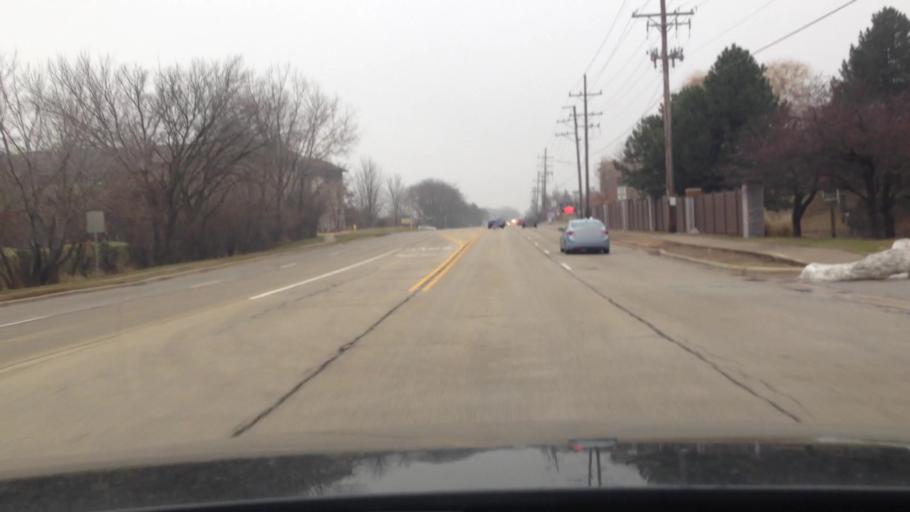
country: US
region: Illinois
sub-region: DuPage County
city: Westmont
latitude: 41.8184
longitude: -87.9763
